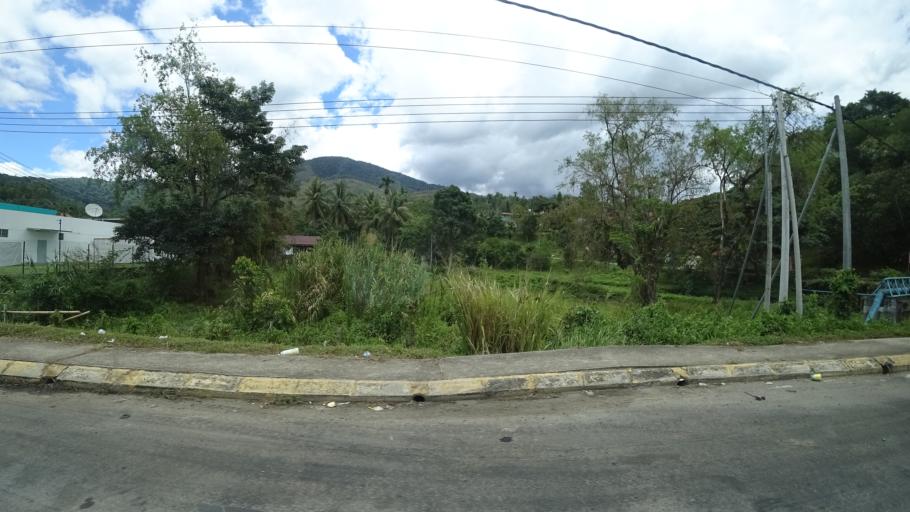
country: MY
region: Sabah
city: Ranau
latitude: 5.9778
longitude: 116.6818
